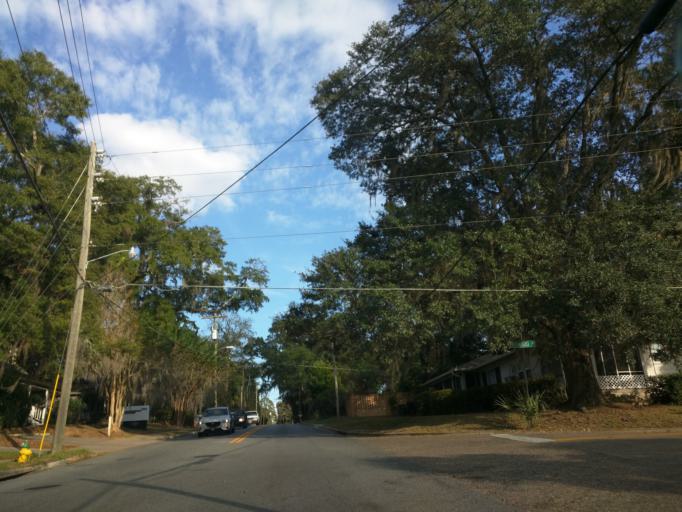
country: US
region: Florida
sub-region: Leon County
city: Tallahassee
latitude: 30.4417
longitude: -84.2701
